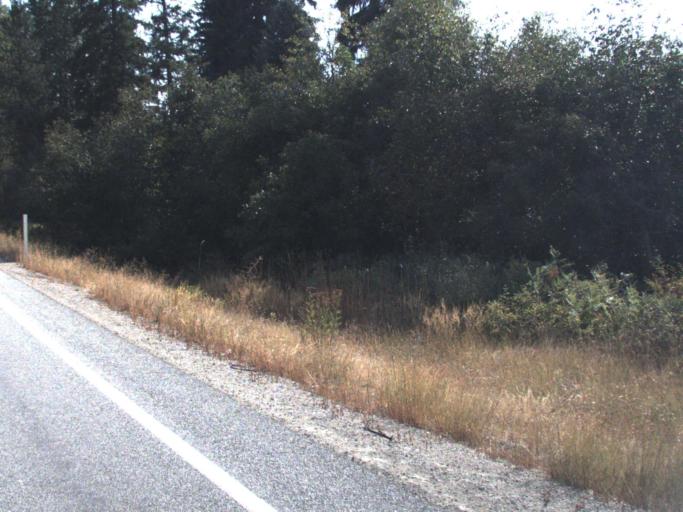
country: US
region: Washington
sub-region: Pend Oreille County
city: Newport
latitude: 48.2093
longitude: -117.2900
